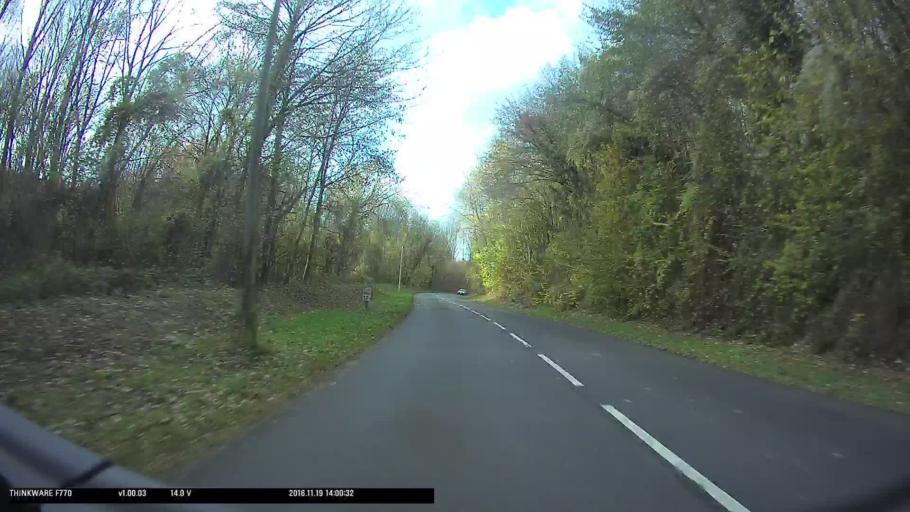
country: FR
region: Ile-de-France
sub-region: Departement du Val-d'Oise
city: Ableiges
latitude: 49.0870
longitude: 1.9955
